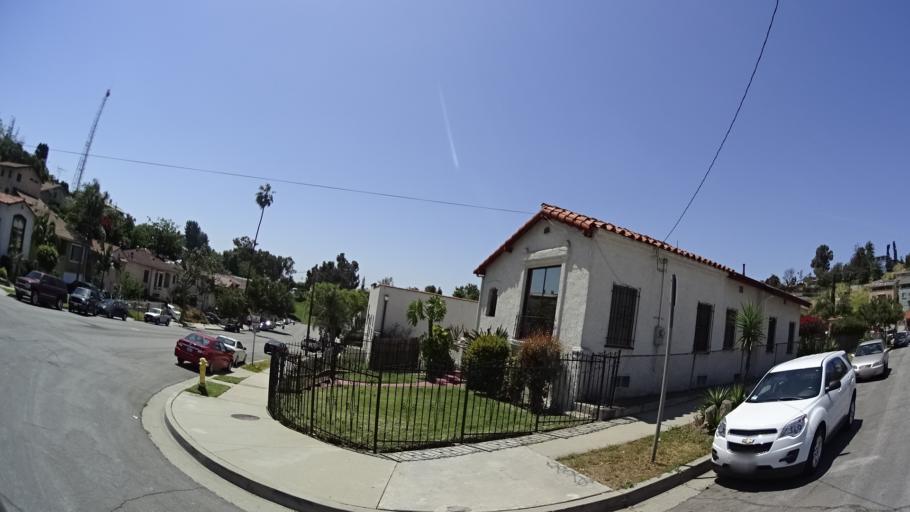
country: US
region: California
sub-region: Los Angeles County
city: Belvedere
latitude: 34.0526
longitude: -118.1777
